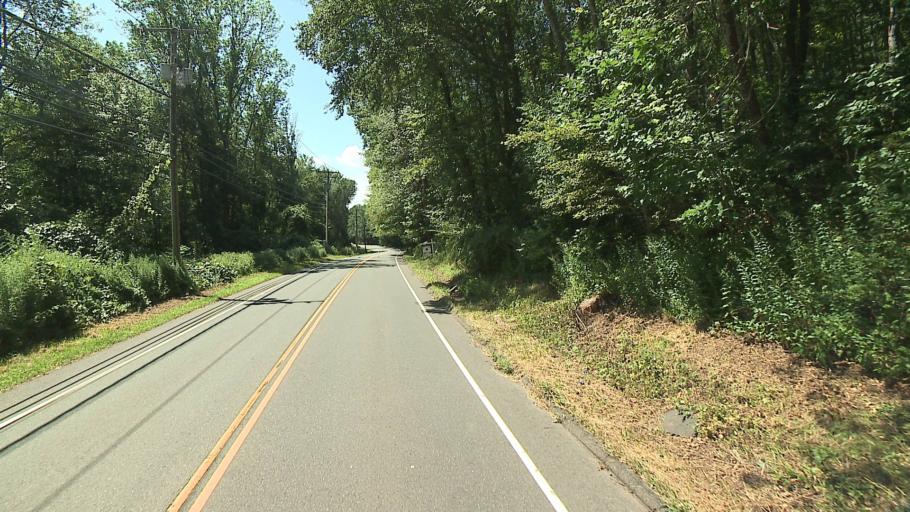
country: US
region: Connecticut
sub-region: New Haven County
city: Oxford
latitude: 41.3578
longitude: -73.1948
